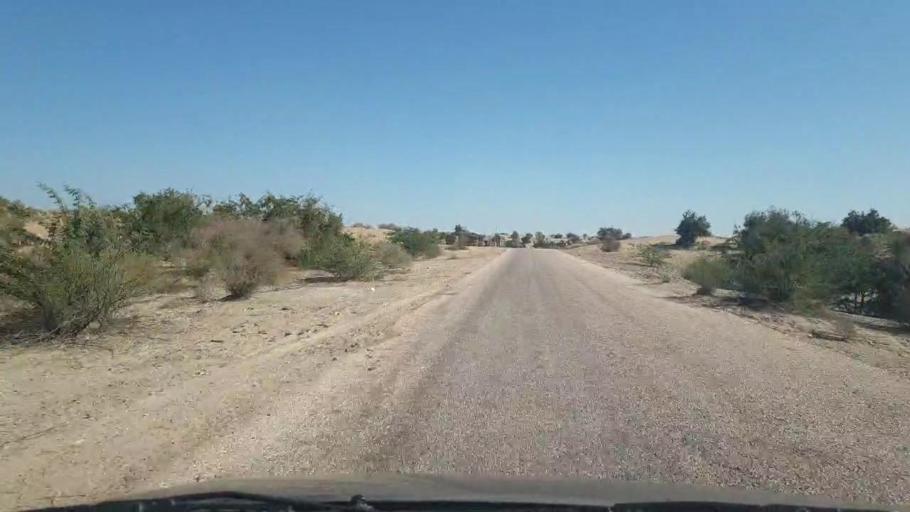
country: PK
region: Sindh
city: Bozdar
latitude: 27.0063
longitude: 68.9045
